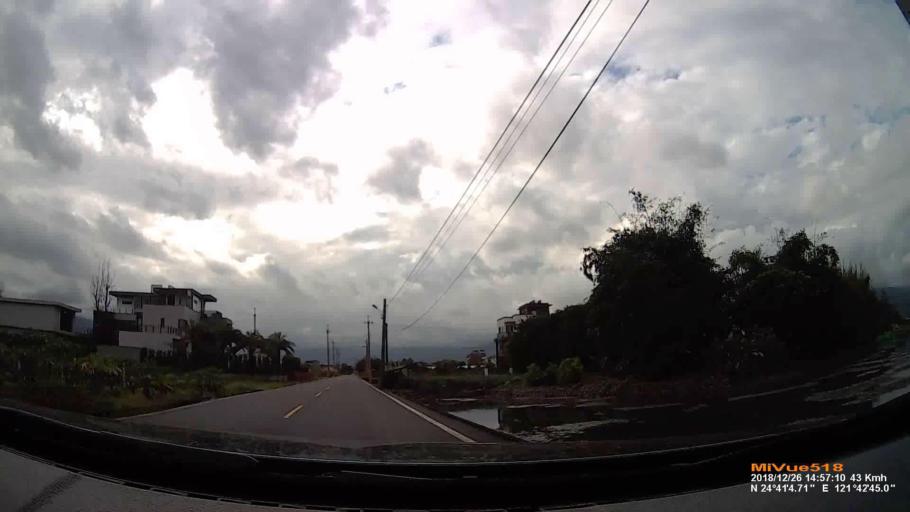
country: TW
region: Taiwan
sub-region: Yilan
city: Yilan
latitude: 24.6846
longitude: 121.7123
